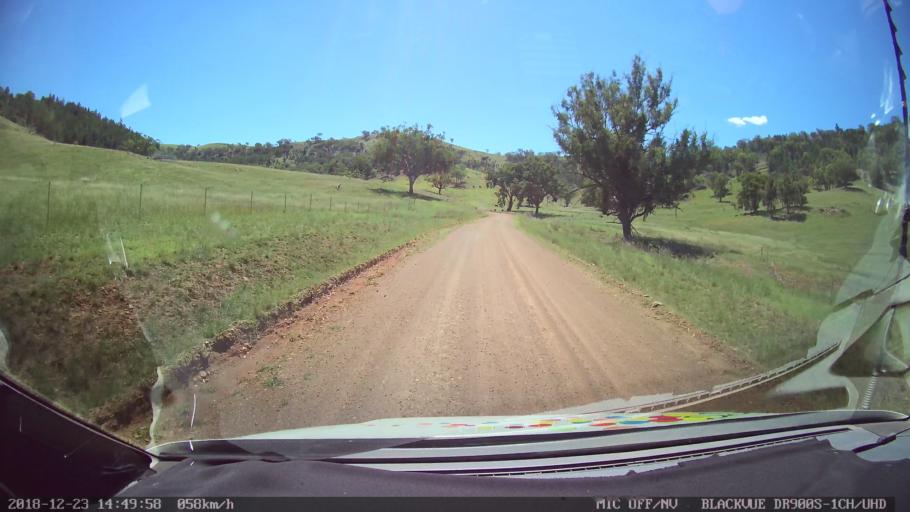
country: AU
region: New South Wales
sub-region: Tamworth Municipality
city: Manilla
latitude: -30.6709
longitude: 150.8605
